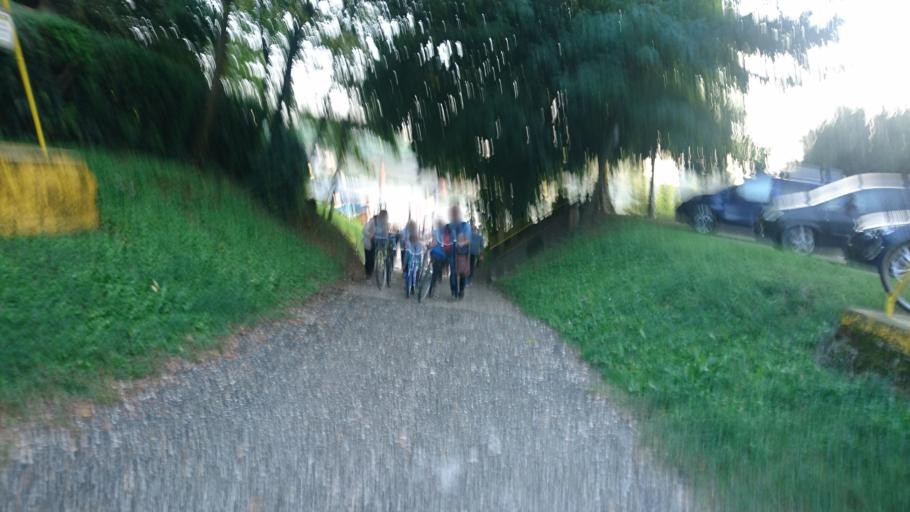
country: IT
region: Veneto
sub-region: Provincia di Rovigo
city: Santa Maria Maddalena
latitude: 44.8901
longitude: 11.6061
